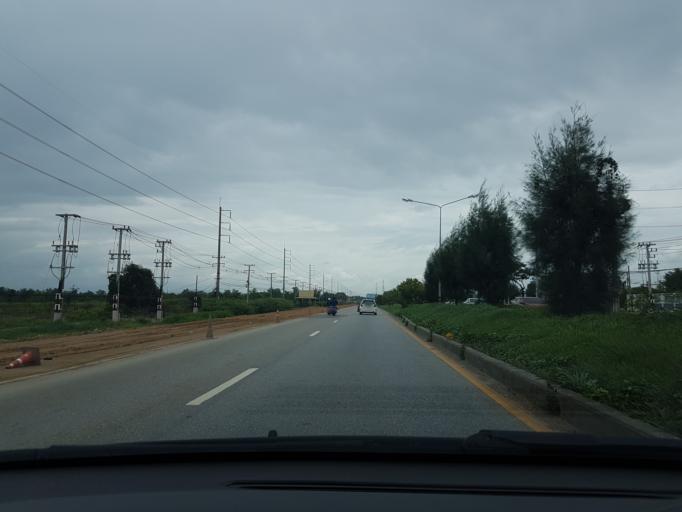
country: TH
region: Lamphun
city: Lamphun
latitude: 18.5751
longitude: 99.0435
